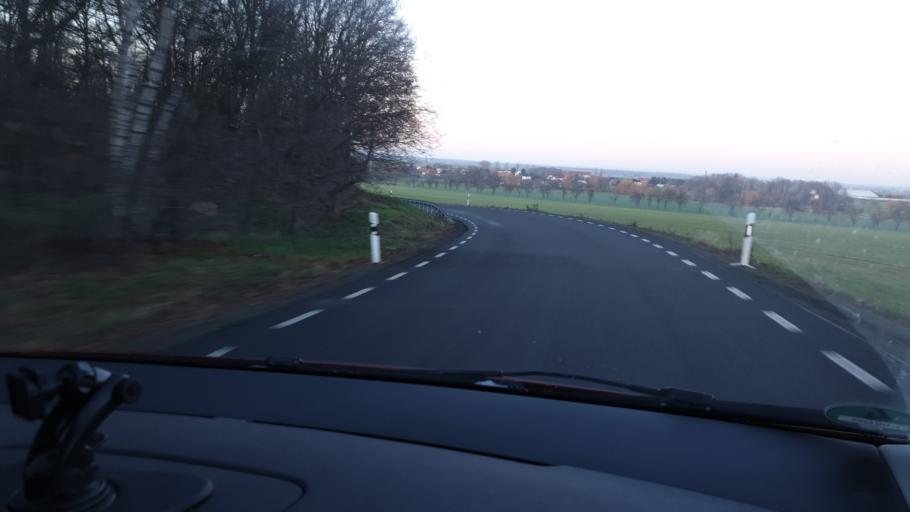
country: DE
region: Saxony
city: Hohburg
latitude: 51.4436
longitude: 12.7858
